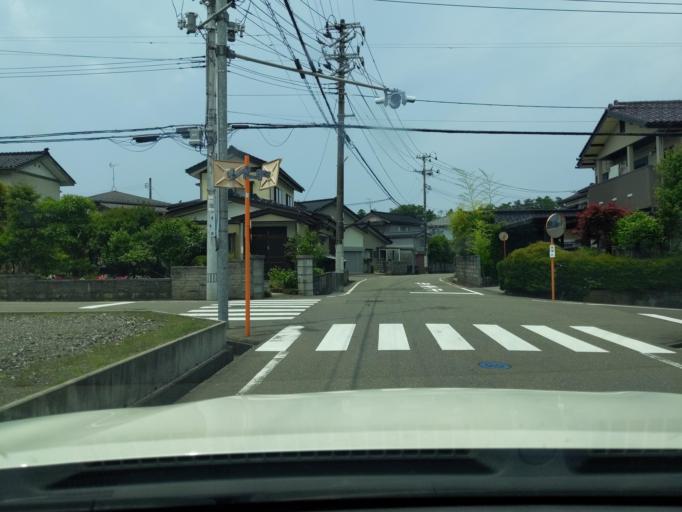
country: JP
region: Niigata
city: Kashiwazaki
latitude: 37.3537
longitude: 138.5417
